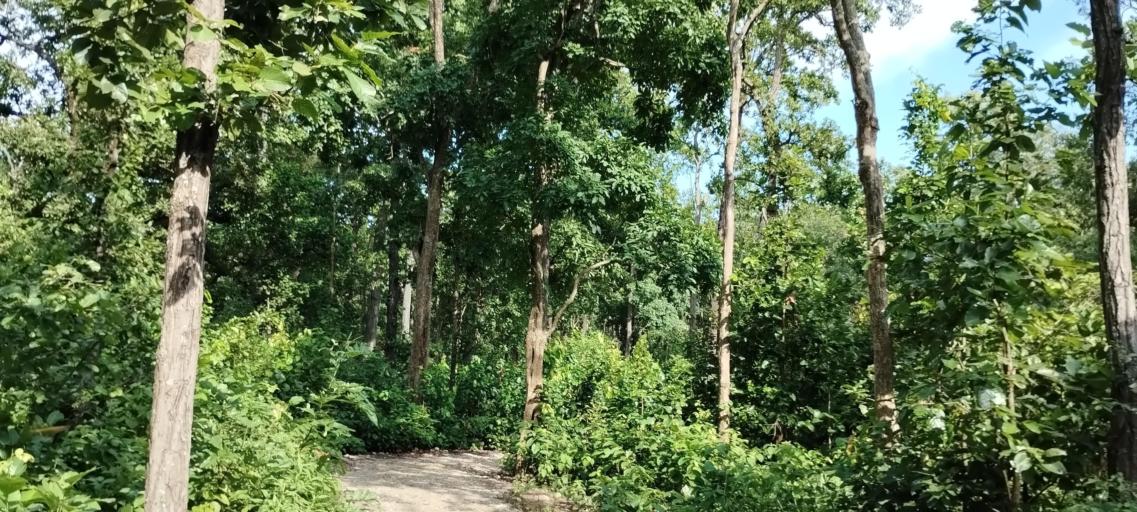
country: NP
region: Far Western
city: Tikapur
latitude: 28.5619
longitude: 81.2661
